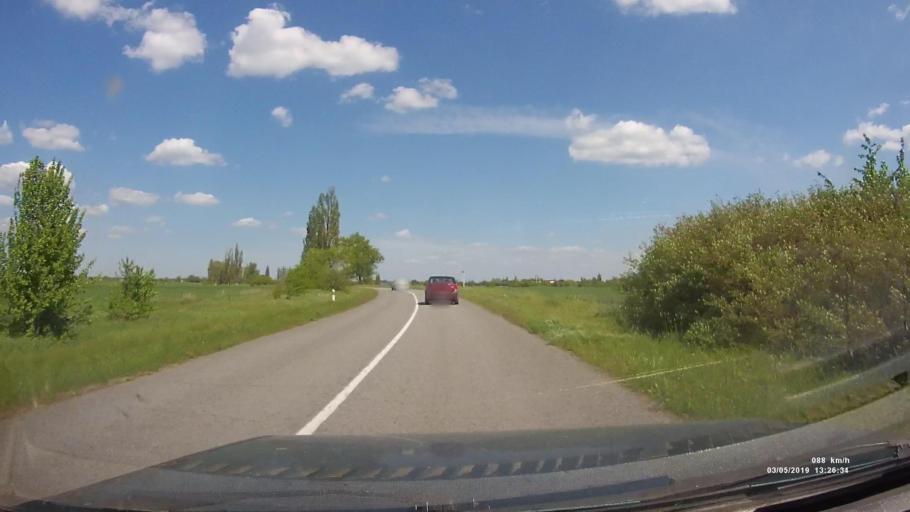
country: RU
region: Rostov
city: Semikarakorsk
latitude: 47.5718
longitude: 40.8229
